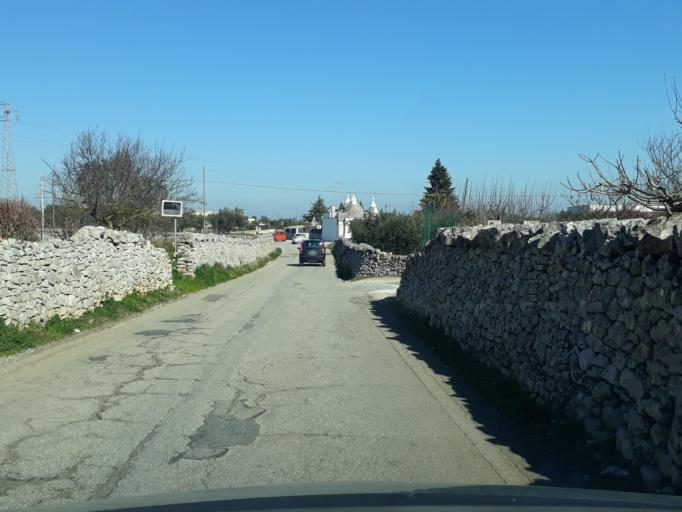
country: IT
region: Apulia
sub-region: Provincia di Taranto
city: Martina Franca
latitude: 40.7217
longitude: 17.3484
